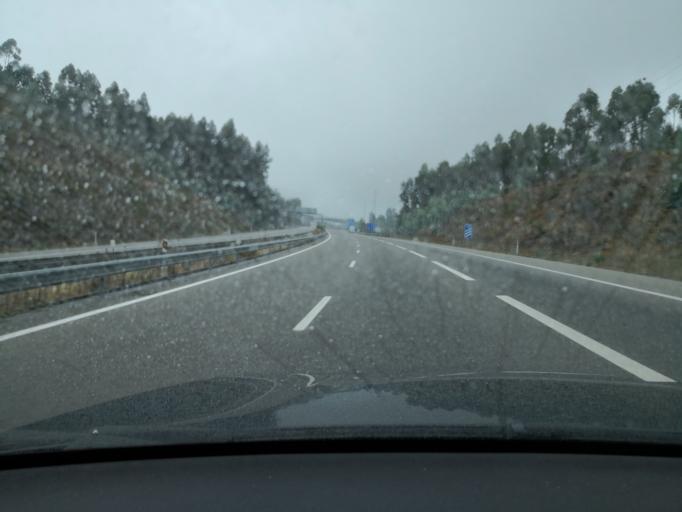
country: PT
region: Porto
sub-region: Pacos de Ferreira
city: Seroa
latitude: 41.2402
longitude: -8.4355
